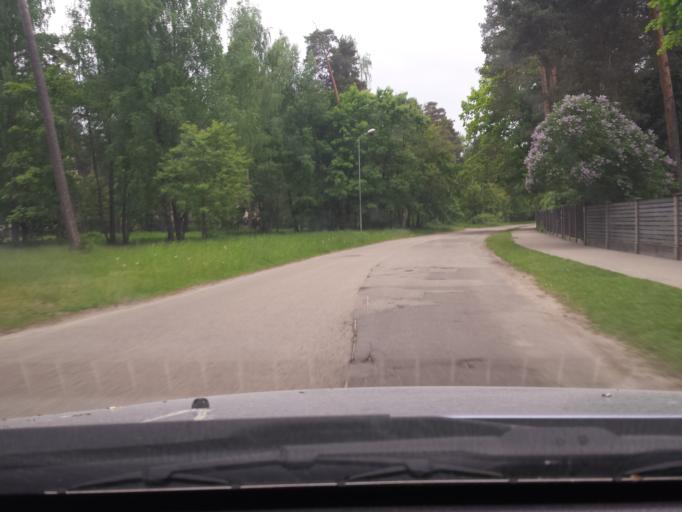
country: LV
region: Riga
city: Jaunciems
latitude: 57.0015
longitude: 24.1559
